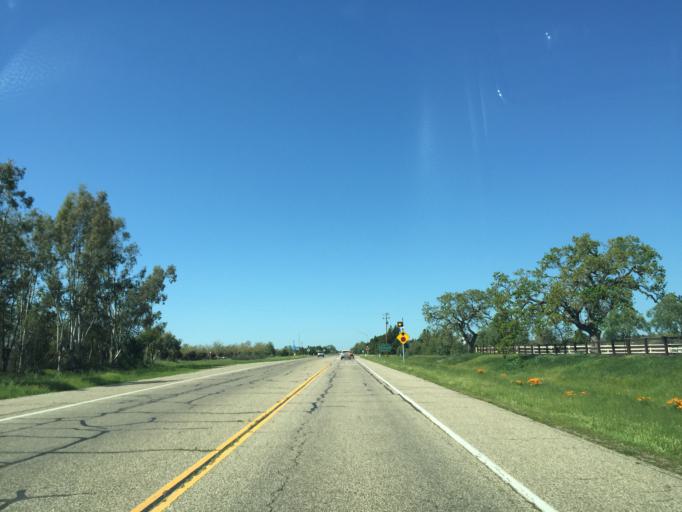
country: US
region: California
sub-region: Santa Barbara County
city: Santa Ynez
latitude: 34.6320
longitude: -120.0795
